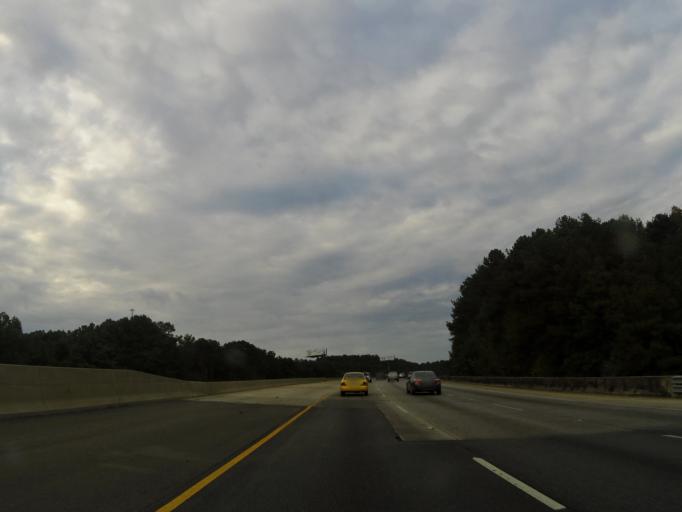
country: US
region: Alabama
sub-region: Shelby County
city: Pelham
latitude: 33.3181
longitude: -86.7869
